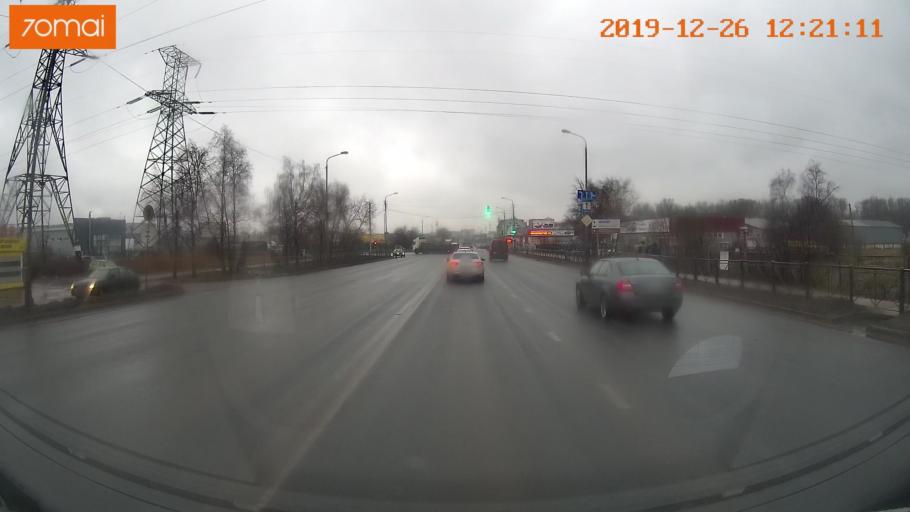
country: RU
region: Vologda
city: Cherepovets
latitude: 59.1529
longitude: 37.9312
